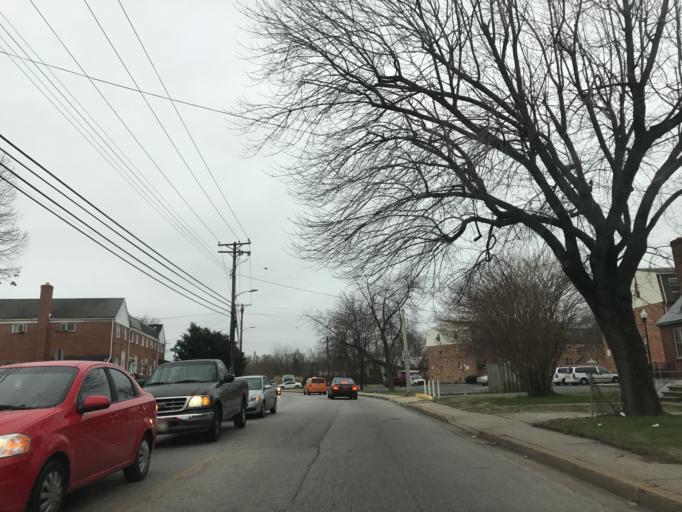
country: US
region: Maryland
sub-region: Baltimore County
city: Rosedale
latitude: 39.3195
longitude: -76.5520
